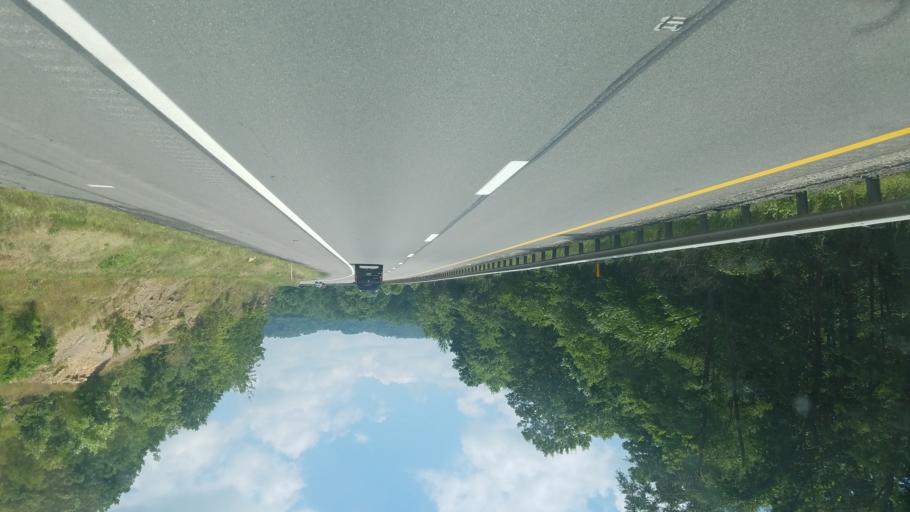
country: US
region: West Virginia
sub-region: Raleigh County
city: Shady Spring
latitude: 37.6971
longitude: -81.1339
